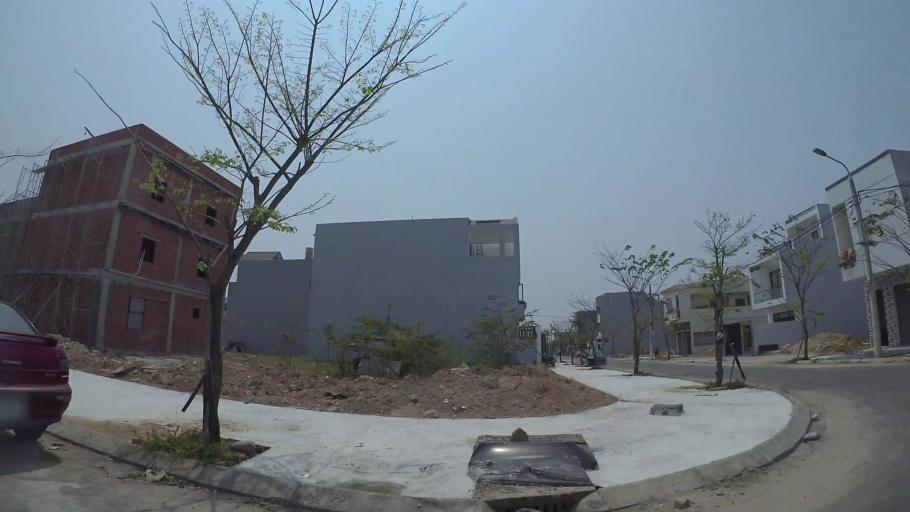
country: VN
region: Da Nang
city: Cam Le
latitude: 16.0179
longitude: 108.2281
